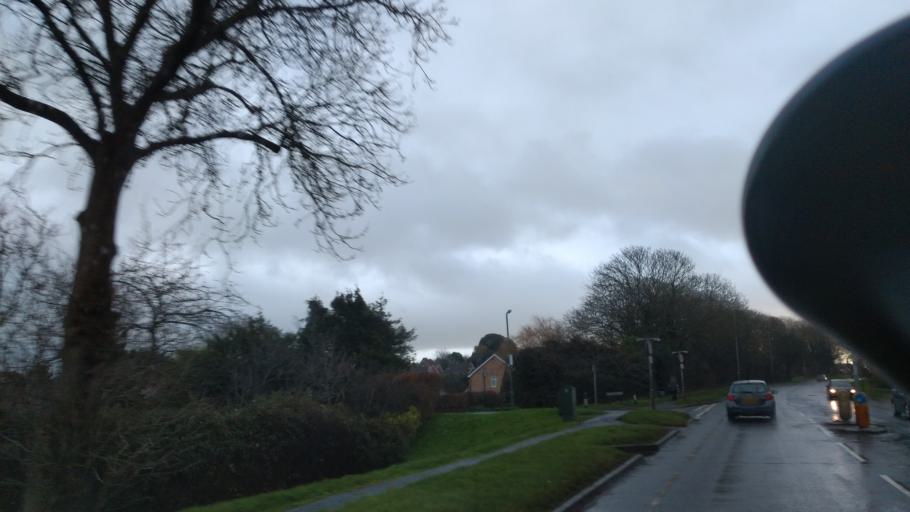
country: GB
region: England
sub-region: East Sussex
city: Eastbourne
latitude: 50.8022
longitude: 0.2521
